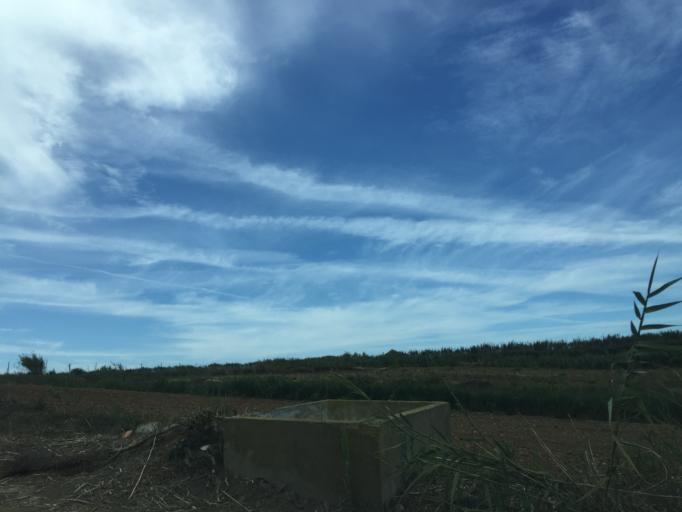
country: PT
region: Lisbon
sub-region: Lourinha
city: Lourinha
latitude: 39.1867
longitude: -9.3472
